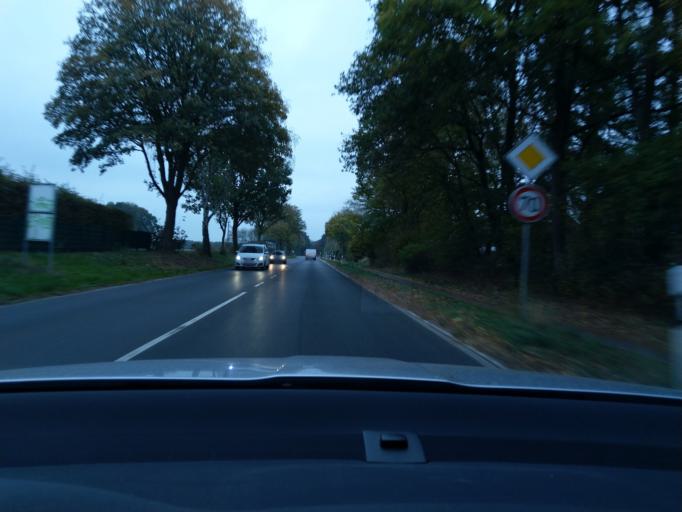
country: DE
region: North Rhine-Westphalia
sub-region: Regierungsbezirk Dusseldorf
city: Schwalmtal
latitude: 51.2085
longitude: 6.2998
